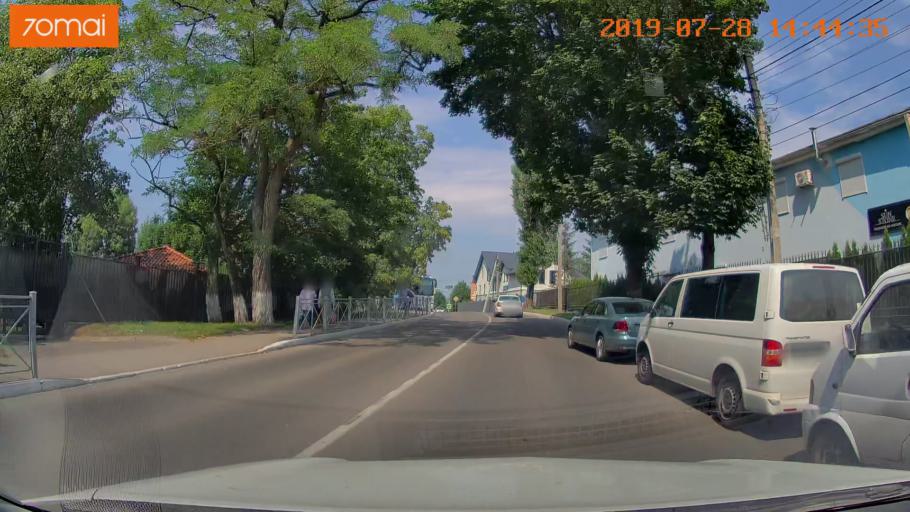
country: RU
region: Kaliningrad
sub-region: Gorod Kaliningrad
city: Yantarnyy
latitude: 54.8681
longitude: 19.9387
